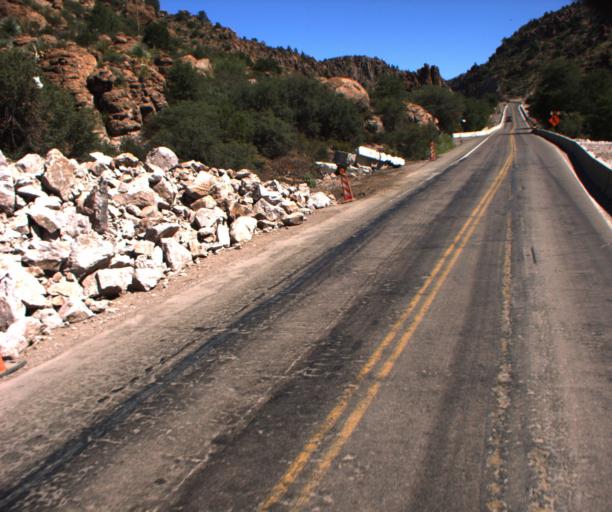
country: US
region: Arizona
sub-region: Pinal County
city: Superior
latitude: 33.3243
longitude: -111.0329
